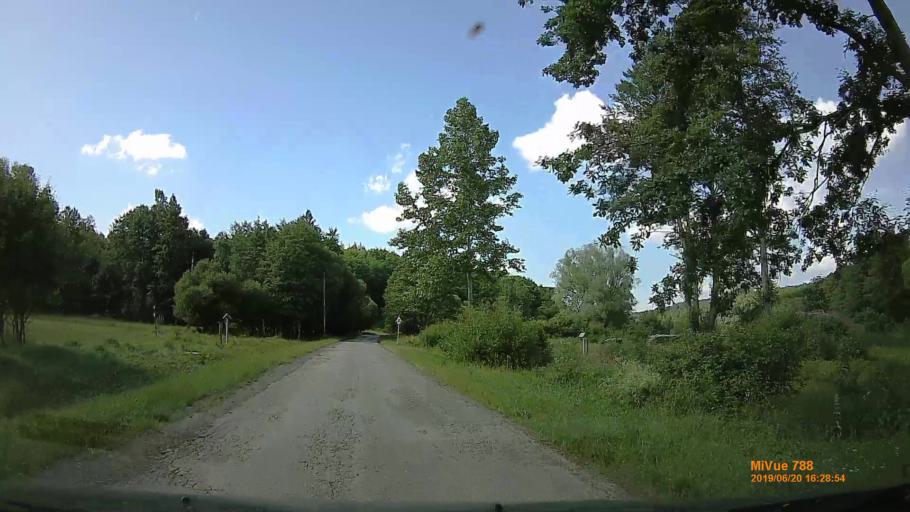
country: HU
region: Baranya
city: Buekkoesd
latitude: 46.1577
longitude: 18.0576
